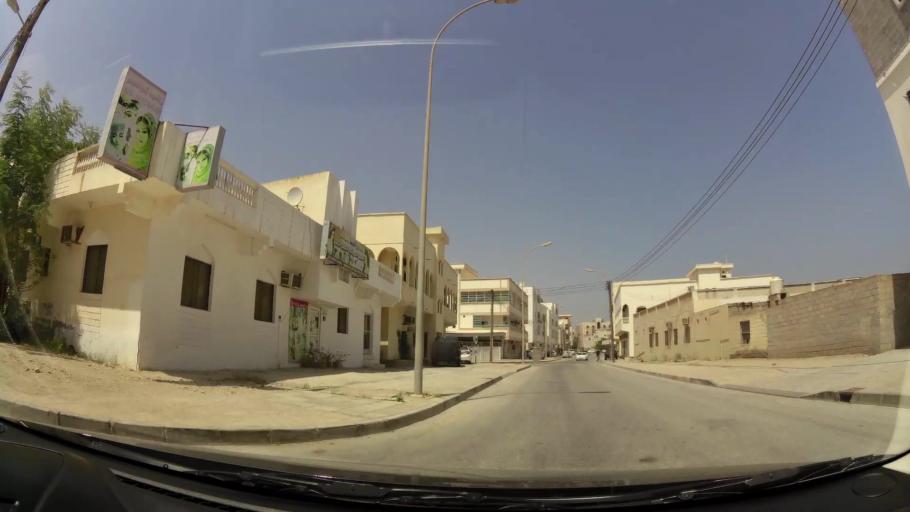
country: OM
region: Zufar
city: Salalah
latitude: 17.0165
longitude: 54.0886
